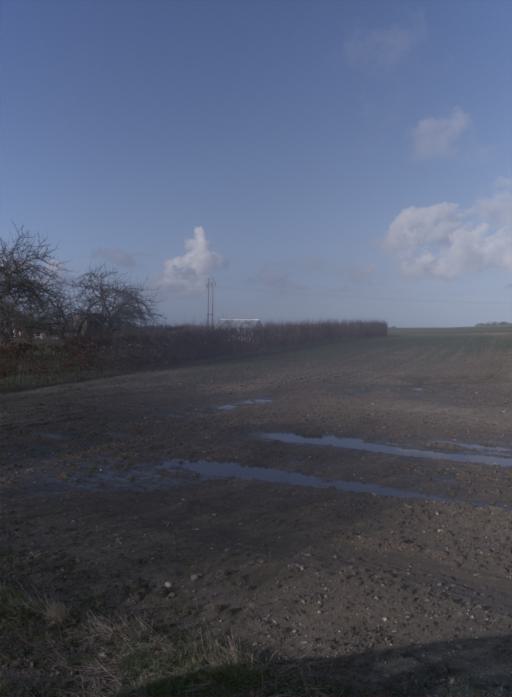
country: DK
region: Zealand
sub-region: Kalundborg Kommune
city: Kalundborg
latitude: 55.6877
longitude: 11.1661
